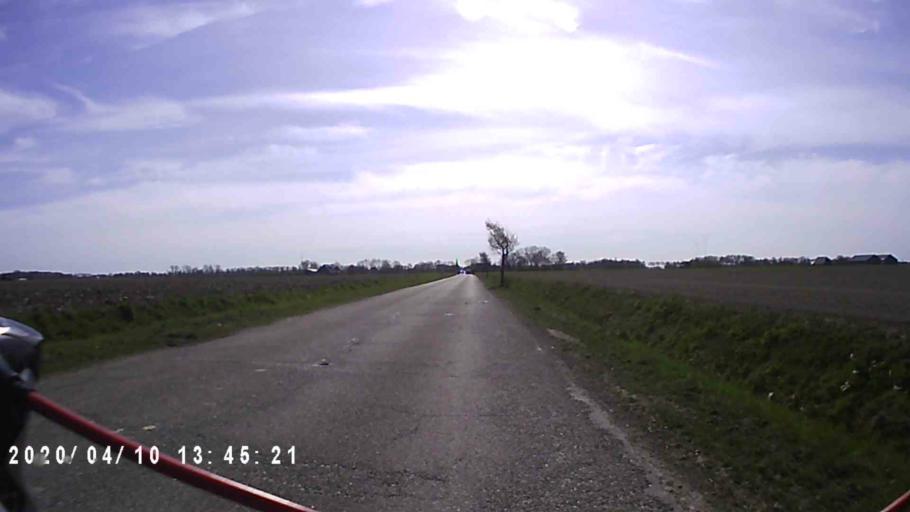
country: NL
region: Groningen
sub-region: Gemeente De Marne
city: Ulrum
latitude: 53.3736
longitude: 6.3747
